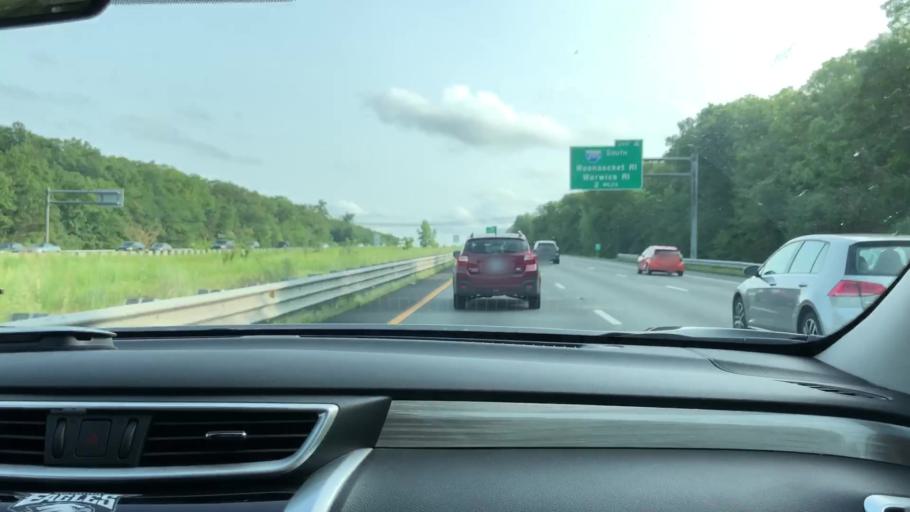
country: US
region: Massachusetts
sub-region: Norfolk County
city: Plainville
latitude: 41.9931
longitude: -71.2930
